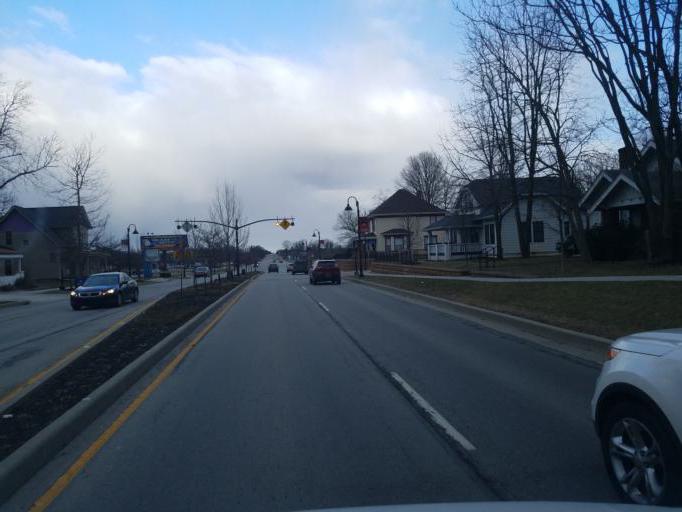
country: US
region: Indiana
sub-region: Marion County
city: Cumberland
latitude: 39.7766
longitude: -85.9546
